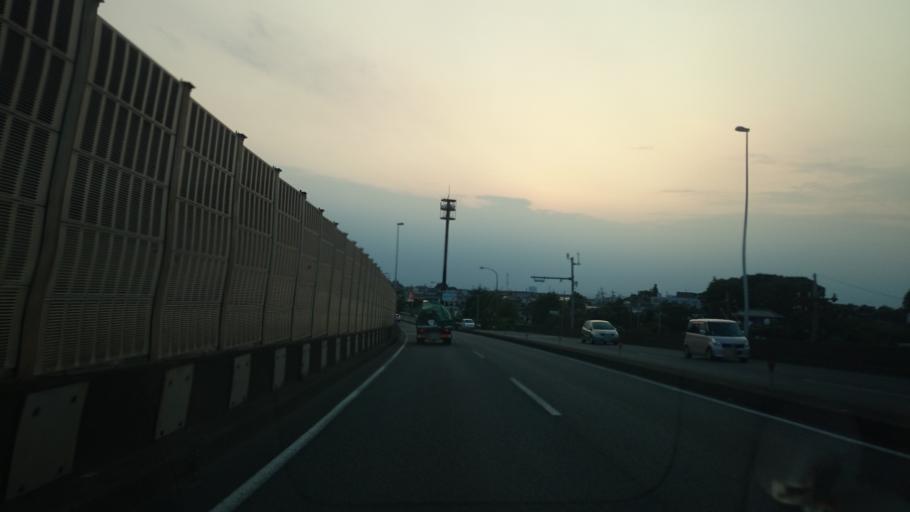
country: JP
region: Saitama
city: Hasuda
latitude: 35.9640
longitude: 139.6416
